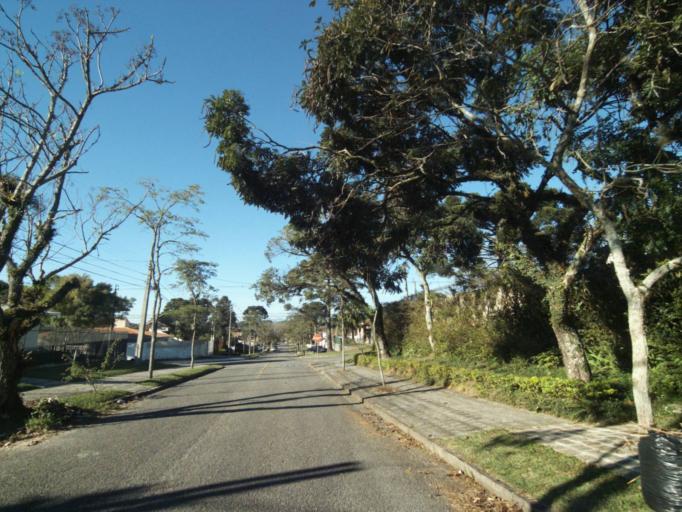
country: BR
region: Parana
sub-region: Curitiba
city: Curitiba
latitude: -25.4225
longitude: -49.2362
